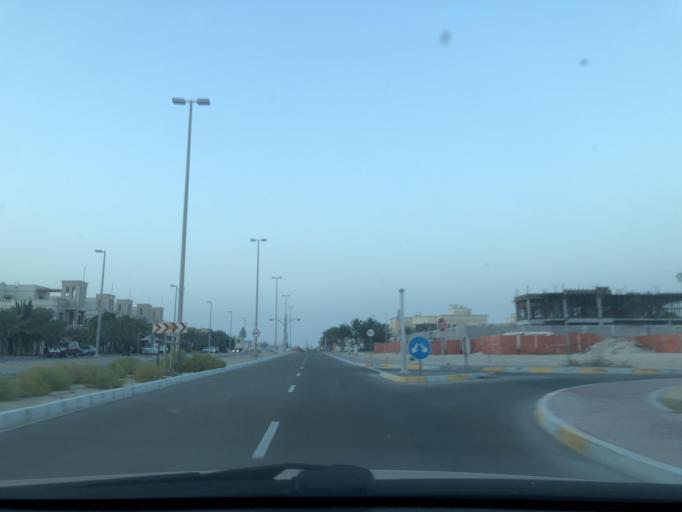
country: AE
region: Abu Dhabi
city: Abu Dhabi
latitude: 24.3514
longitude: 54.6237
